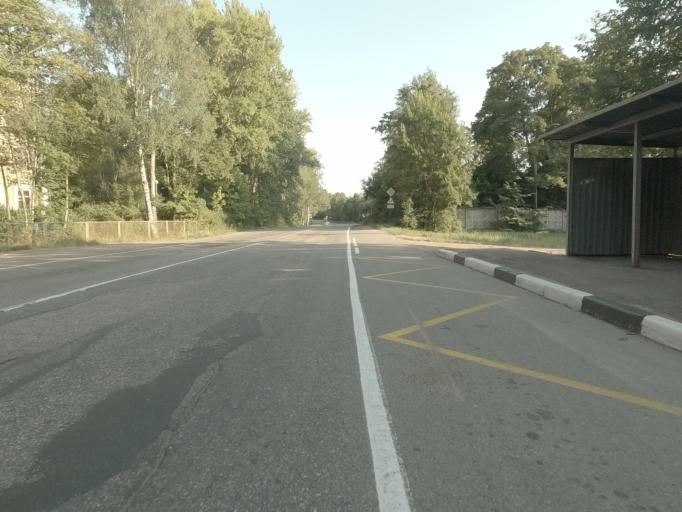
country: RU
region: Leningrad
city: Vyborg
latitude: 60.7318
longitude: 28.7592
